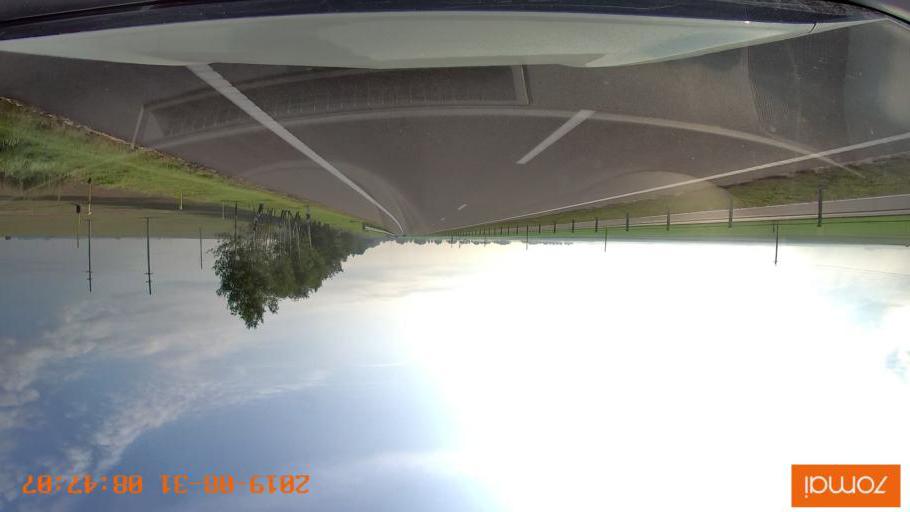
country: BY
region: Minsk
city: Luhavaya Slabada
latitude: 53.7731
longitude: 27.8576
